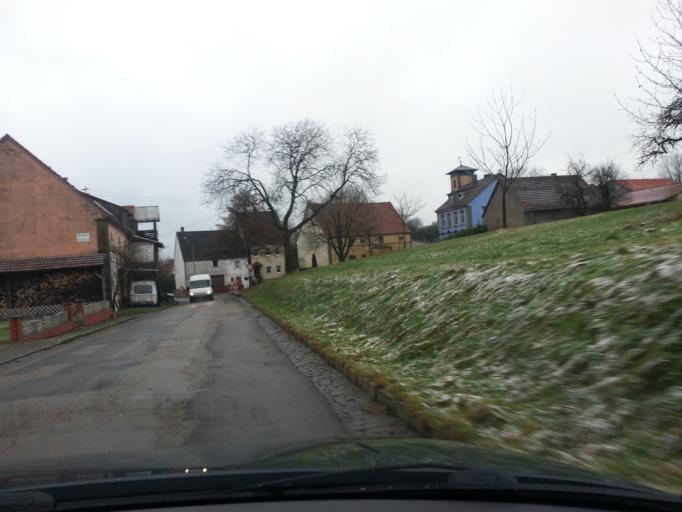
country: DE
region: Rheinland-Pfalz
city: Albessen
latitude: 49.5167
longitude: 7.3297
